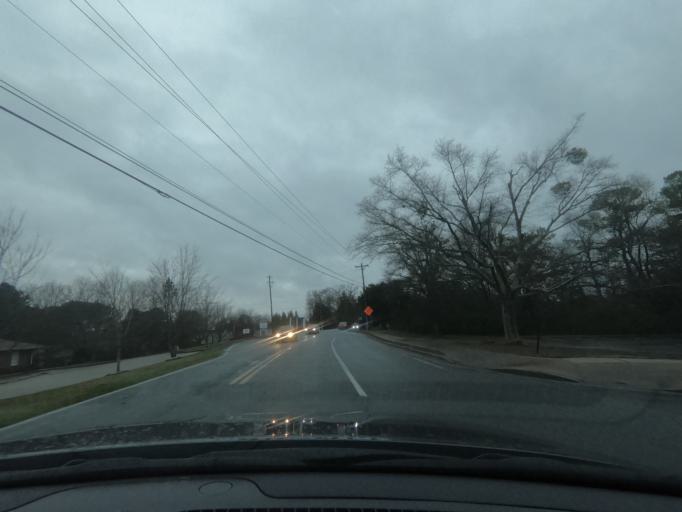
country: US
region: Georgia
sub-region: Cherokee County
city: Woodstock
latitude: 34.0933
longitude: -84.4929
